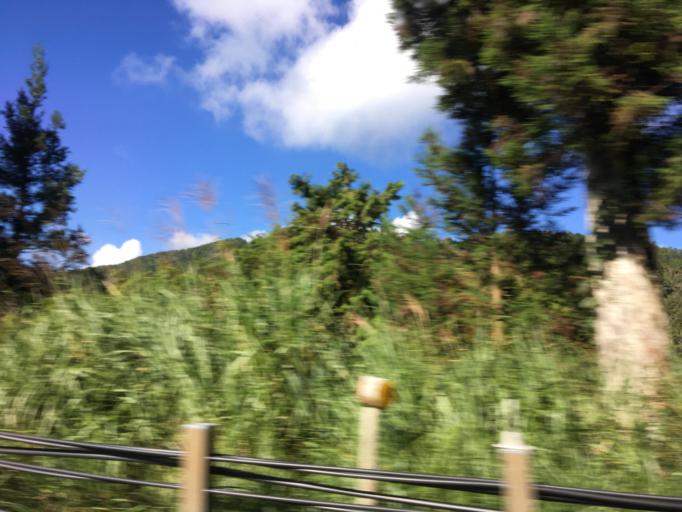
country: TW
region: Taiwan
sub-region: Yilan
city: Yilan
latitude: 24.5036
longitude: 121.5561
